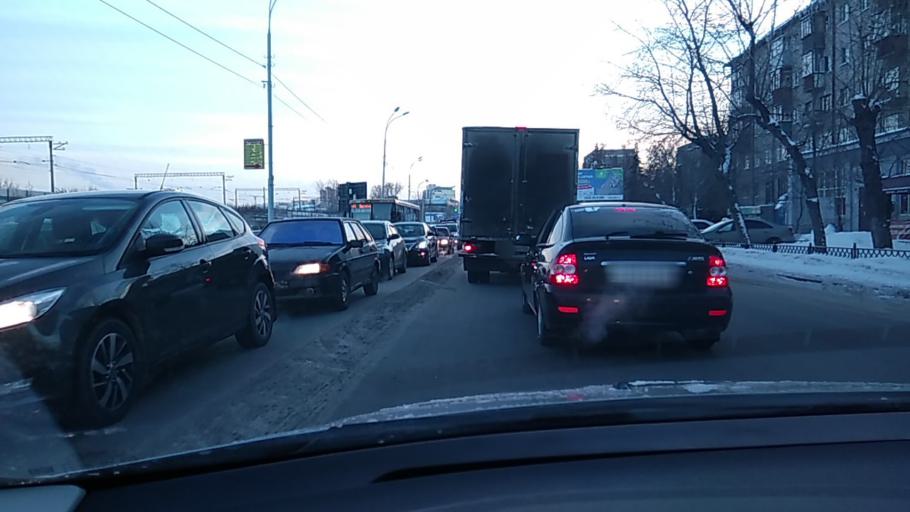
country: RU
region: Sverdlovsk
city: Yekaterinburg
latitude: 56.8394
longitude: 60.6327
